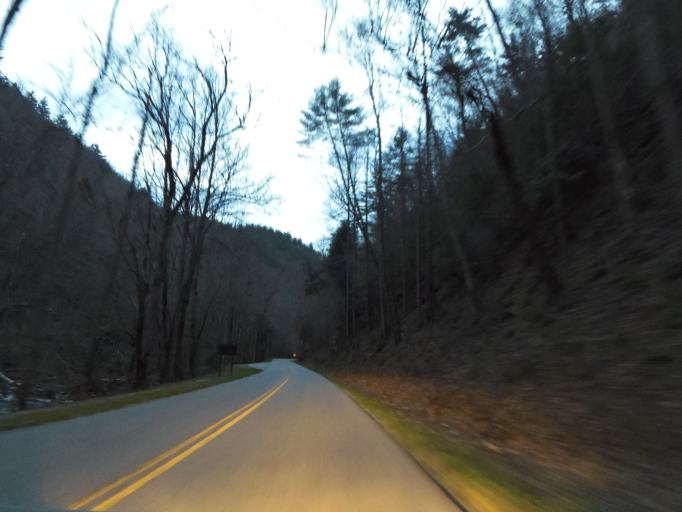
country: US
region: Tennessee
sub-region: Sevier County
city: Pigeon Forge
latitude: 35.6543
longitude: -83.7101
